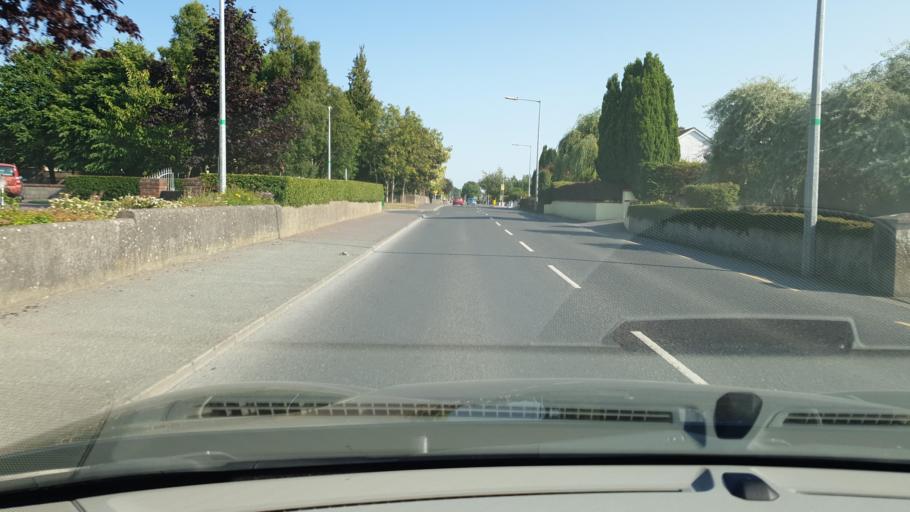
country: IE
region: Leinster
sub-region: An Mhi
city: Navan
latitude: 53.6600
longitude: -6.6882
